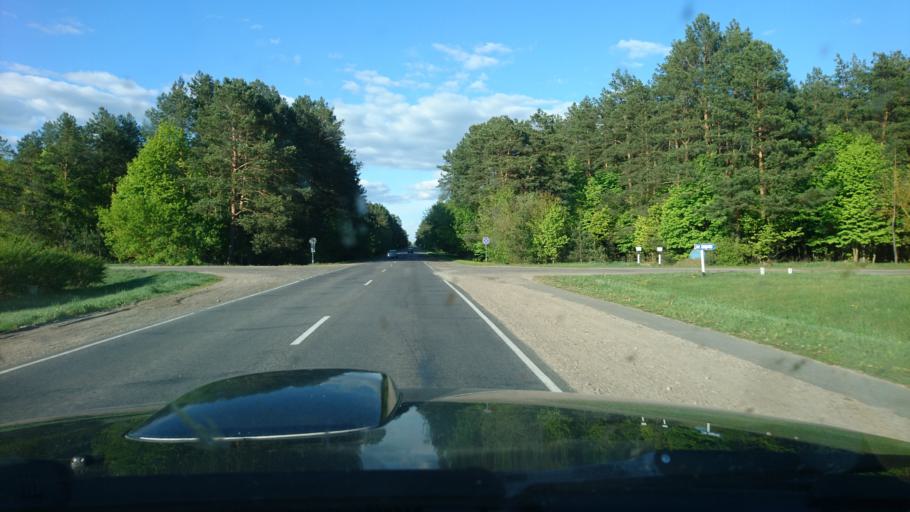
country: BY
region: Brest
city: Ivatsevichy
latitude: 52.7280
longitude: 25.3759
